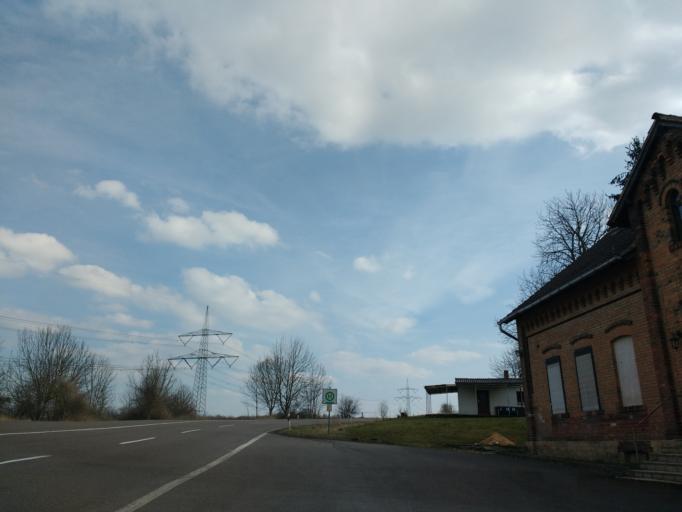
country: DE
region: Saxony-Anhalt
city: Schraplau
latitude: 51.4319
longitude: 11.6508
